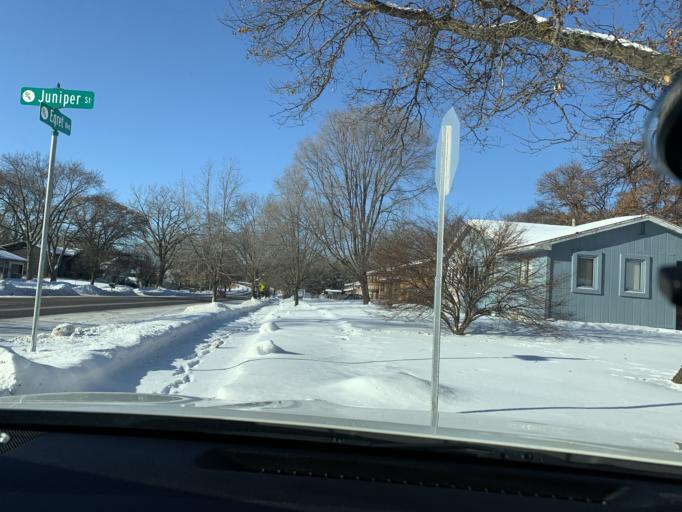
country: US
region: Minnesota
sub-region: Anoka County
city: Coon Rapids
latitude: 45.1639
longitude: -93.2798
